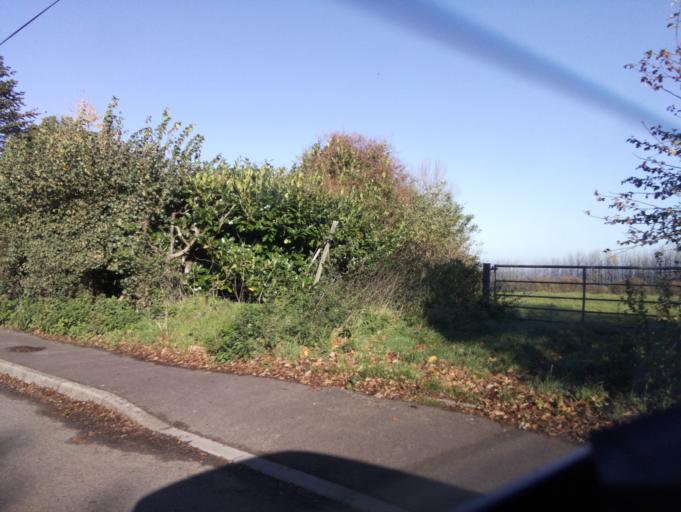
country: GB
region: England
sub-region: Somerset
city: Yeovil
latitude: 50.9572
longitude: -2.6529
